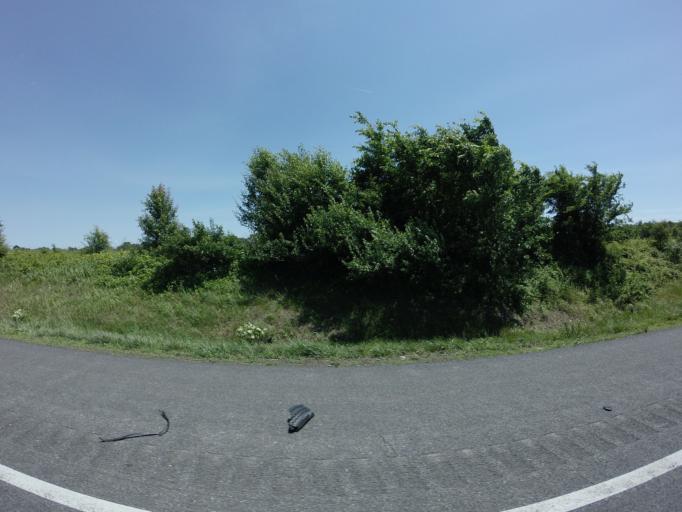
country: US
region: Maryland
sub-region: Frederick County
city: Ballenger Creek
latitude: 39.3834
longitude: -77.4623
